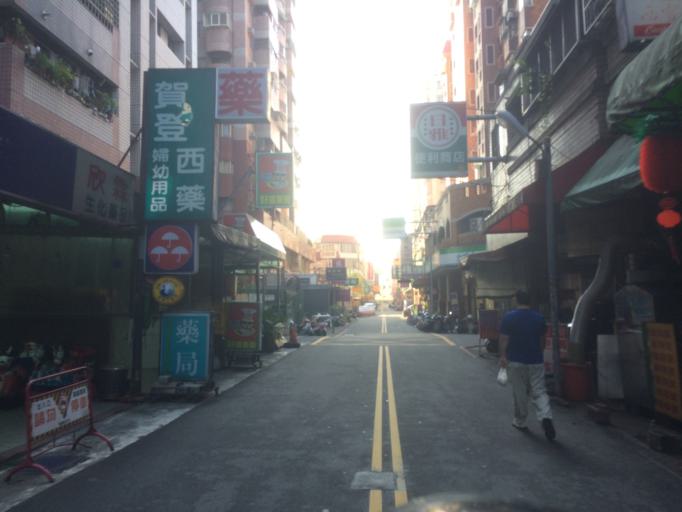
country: TW
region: Taiwan
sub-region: Taichung City
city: Taichung
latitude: 24.1892
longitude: 120.7018
